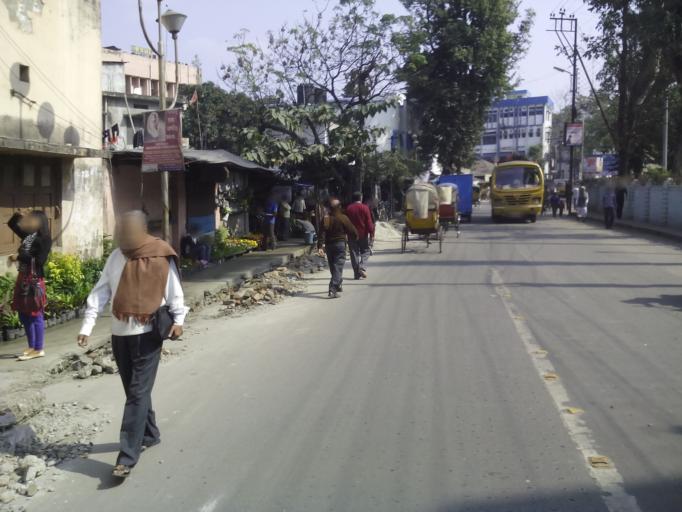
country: IN
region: West Bengal
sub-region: Darjiling
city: Shiliguri
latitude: 26.7111
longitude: 88.4265
